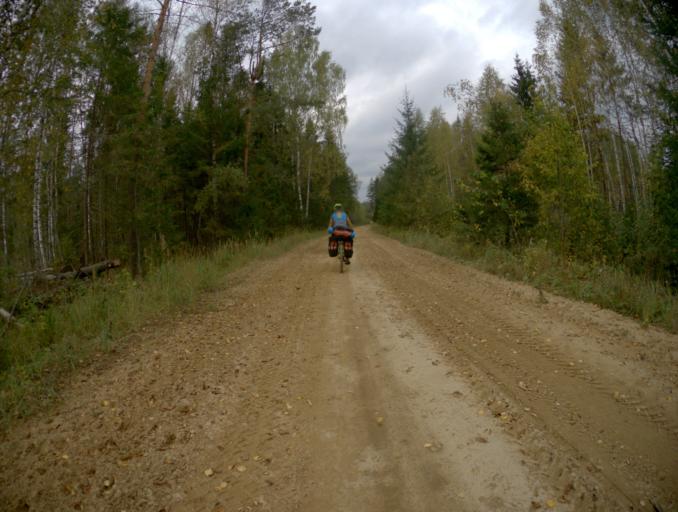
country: RU
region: Vladimir
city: Kideksha
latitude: 56.4691
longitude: 40.6982
